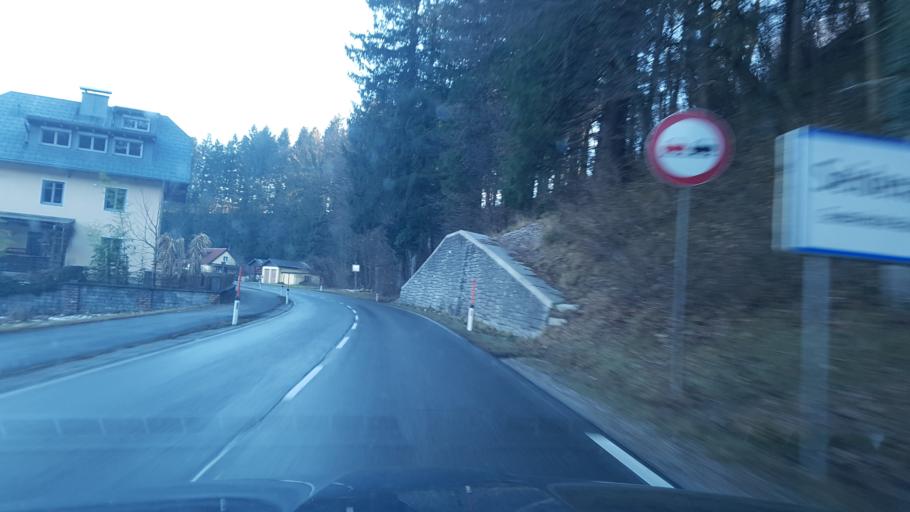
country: AT
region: Salzburg
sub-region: Politischer Bezirk Hallein
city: Adnet
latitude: 47.7000
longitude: 13.1220
